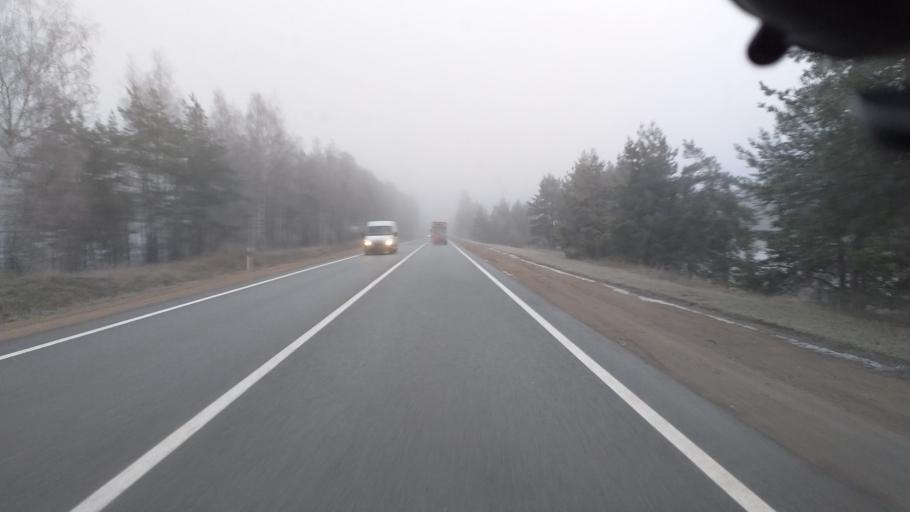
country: LV
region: Marupe
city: Marupe
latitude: 56.8480
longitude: 24.0116
